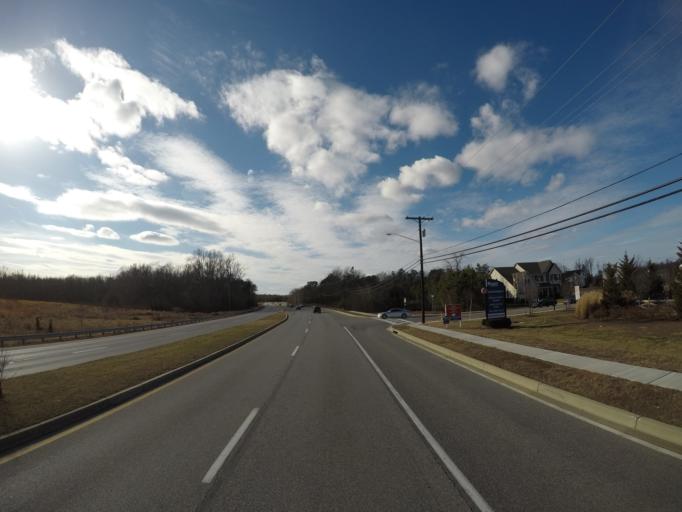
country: US
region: Maryland
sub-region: Charles County
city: Saint Charles
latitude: 38.6103
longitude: -76.9649
